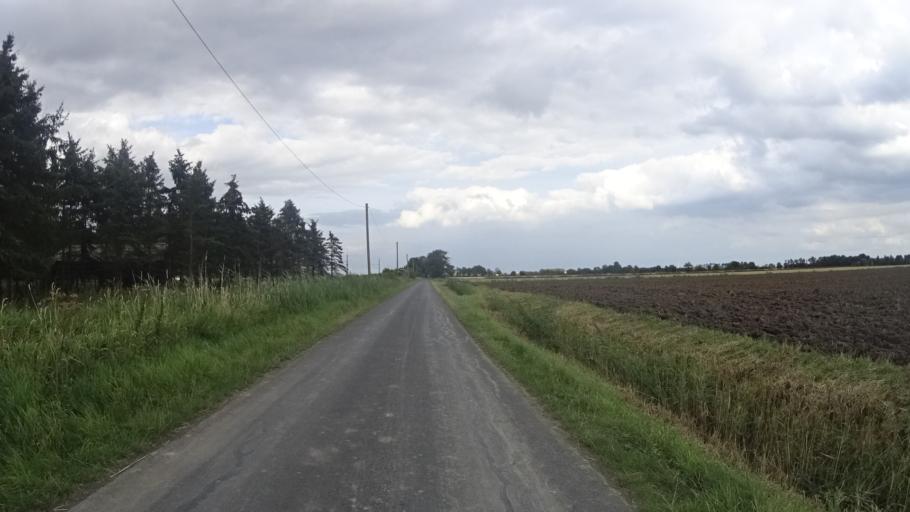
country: DE
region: Schleswig-Holstein
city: Herzhorn
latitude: 53.7804
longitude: 9.4573
